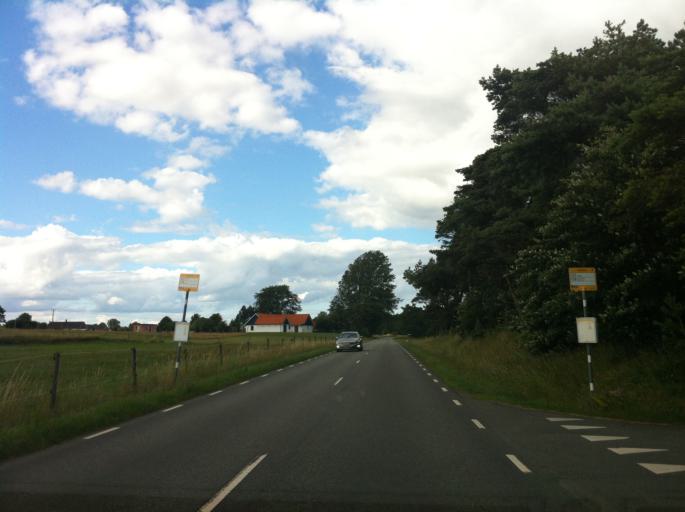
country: SE
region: Skane
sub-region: Simrishamns Kommun
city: Simrishamn
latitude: 55.4190
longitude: 14.2103
